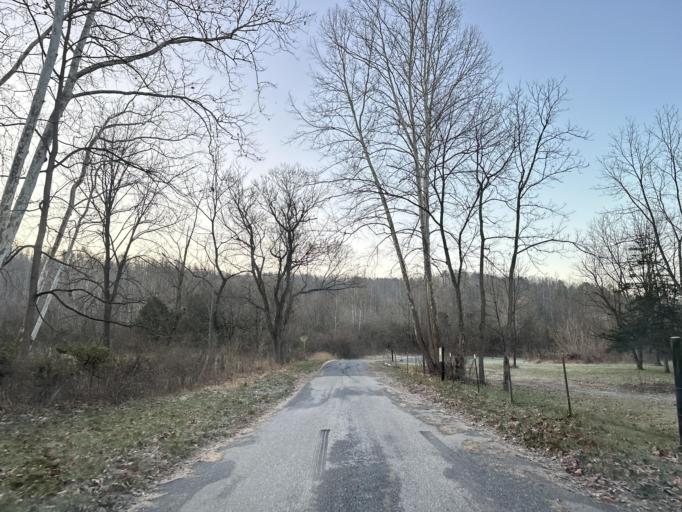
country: US
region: Virginia
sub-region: Rockbridge County
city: East Lexington
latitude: 38.0777
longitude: -79.3678
